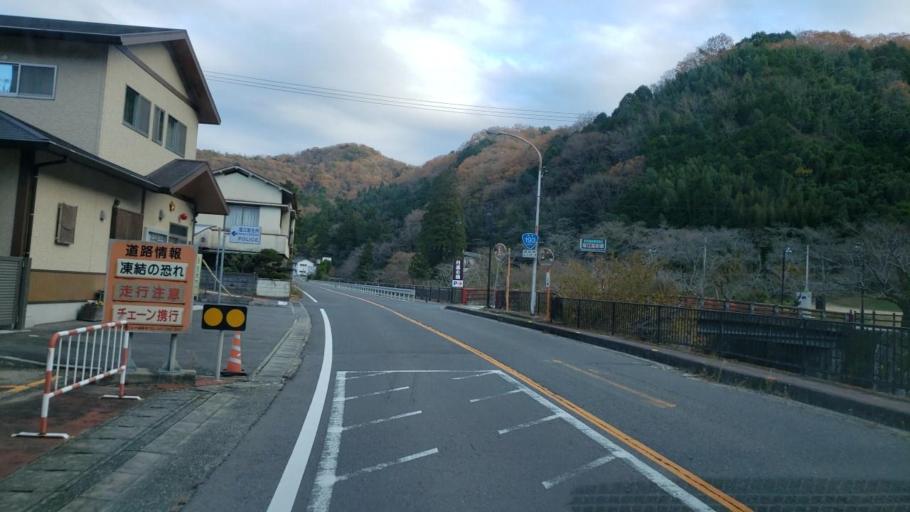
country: JP
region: Tokushima
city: Wakimachi
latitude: 34.1696
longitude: 134.0829
